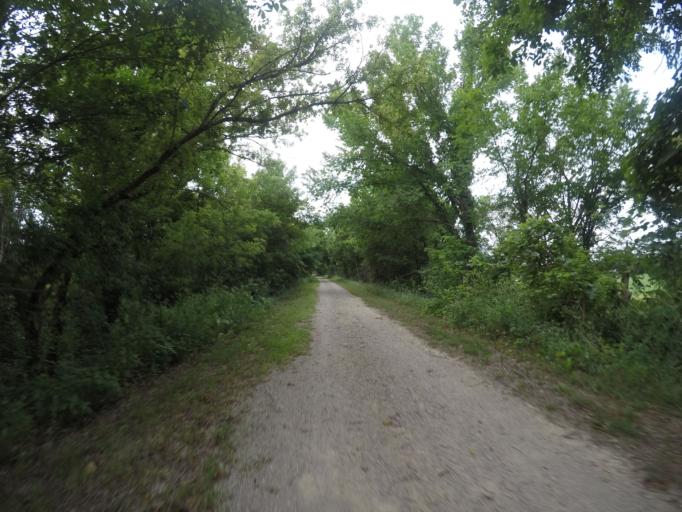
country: US
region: Kansas
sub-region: Franklin County
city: Ottawa
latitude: 38.4789
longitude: -95.2750
